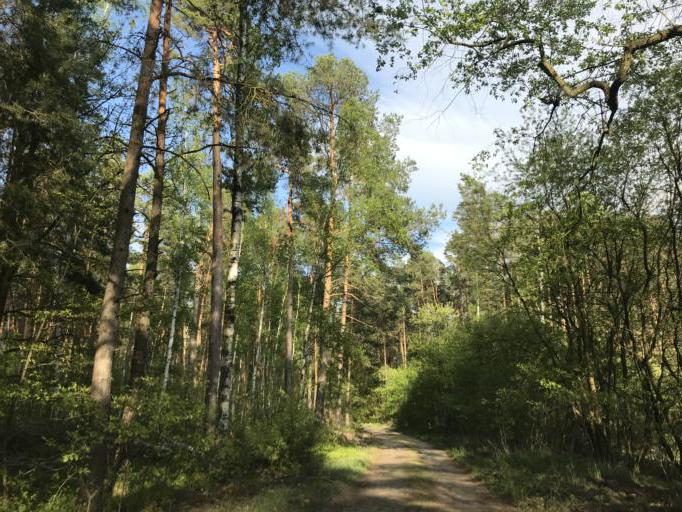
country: DE
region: Brandenburg
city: Joachimsthal
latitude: 52.9631
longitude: 13.7068
